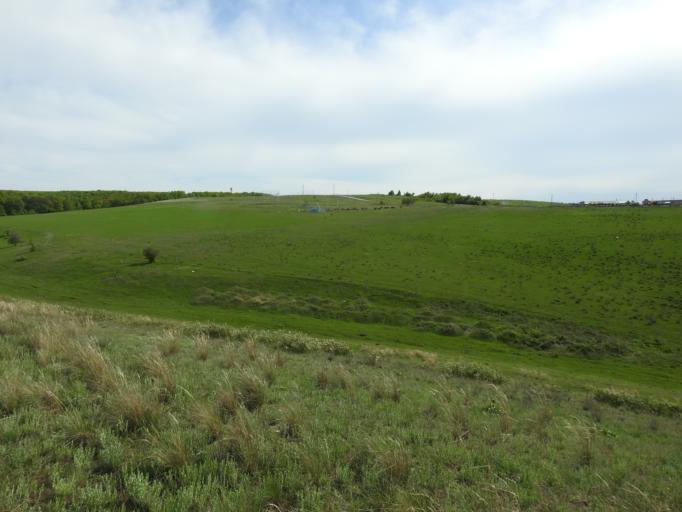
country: RU
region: Saratov
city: Krasnyy Oktyabr'
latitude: 51.5630
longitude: 45.7106
